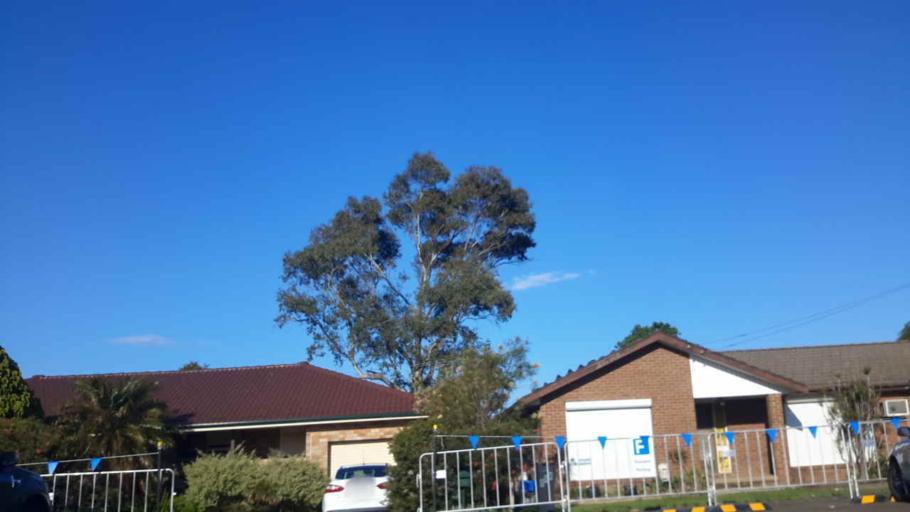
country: AU
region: New South Wales
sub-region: Penrith Municipality
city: Kingswood Park
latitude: -33.7729
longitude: 150.7117
